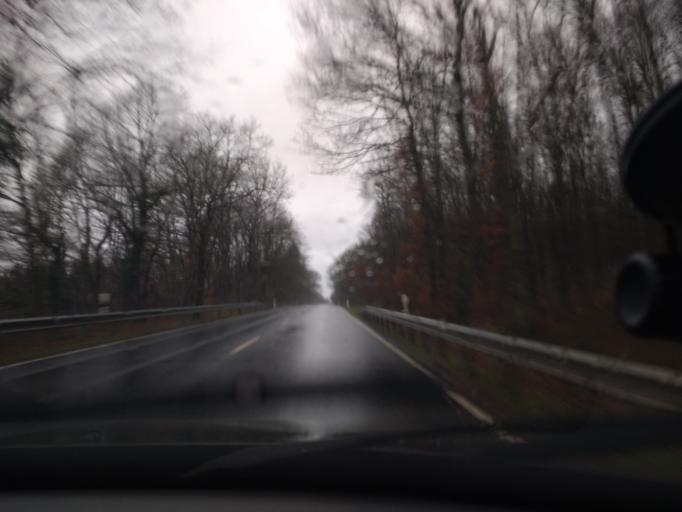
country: DE
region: Rheinland-Pfalz
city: Pellingen
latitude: 49.6998
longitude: 6.6391
